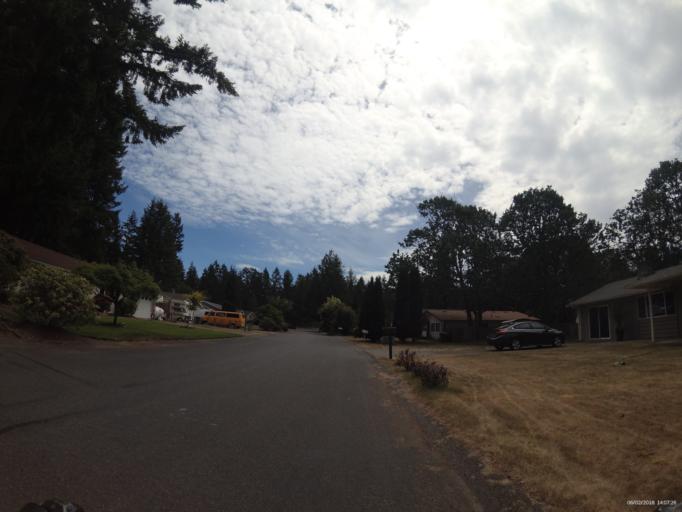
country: US
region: Washington
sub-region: Pierce County
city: University Place
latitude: 47.2074
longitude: -122.5632
